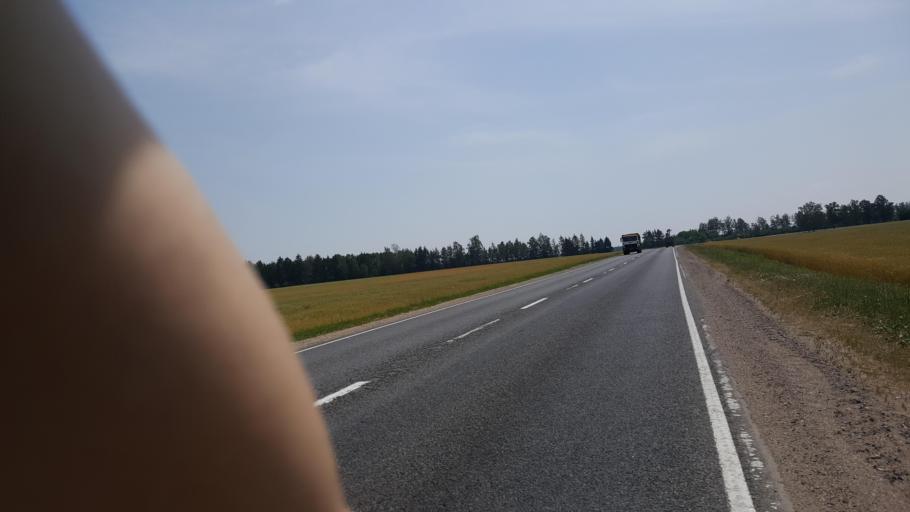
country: BY
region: Brest
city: Kamyanyets
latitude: 52.3754
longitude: 23.7915
